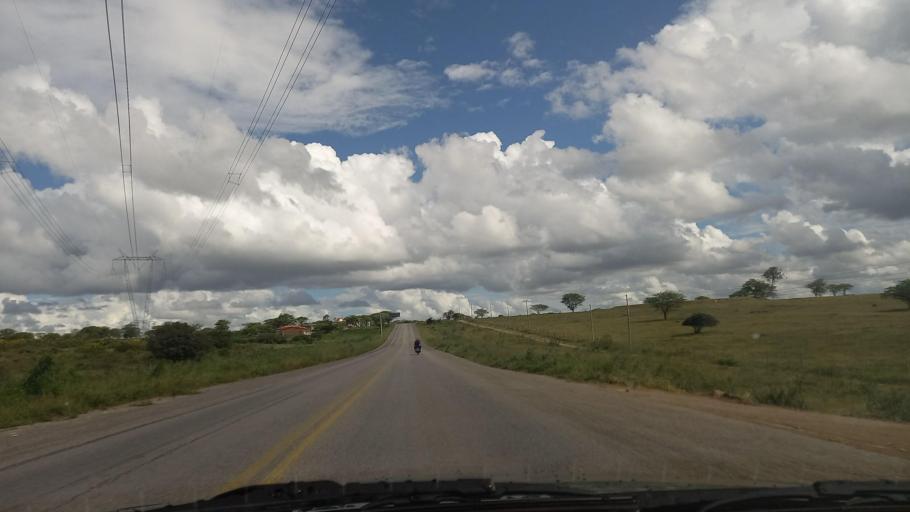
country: BR
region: Pernambuco
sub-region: Lajedo
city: Lajedo
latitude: -8.6027
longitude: -36.2928
